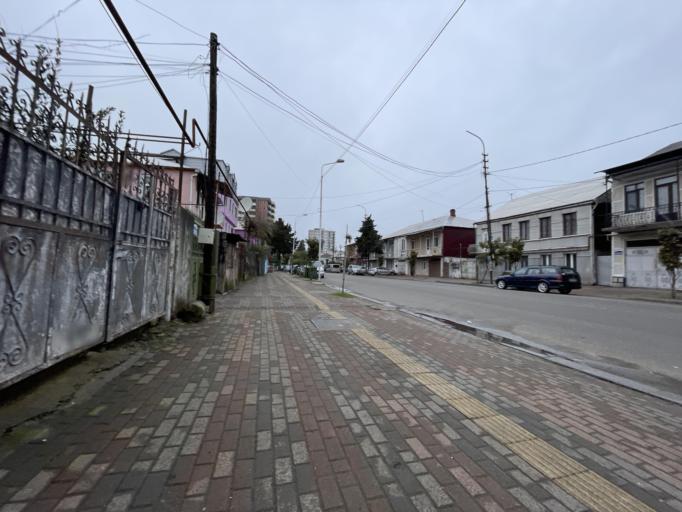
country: GE
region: Ajaria
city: Batumi
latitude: 41.6385
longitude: 41.6425
